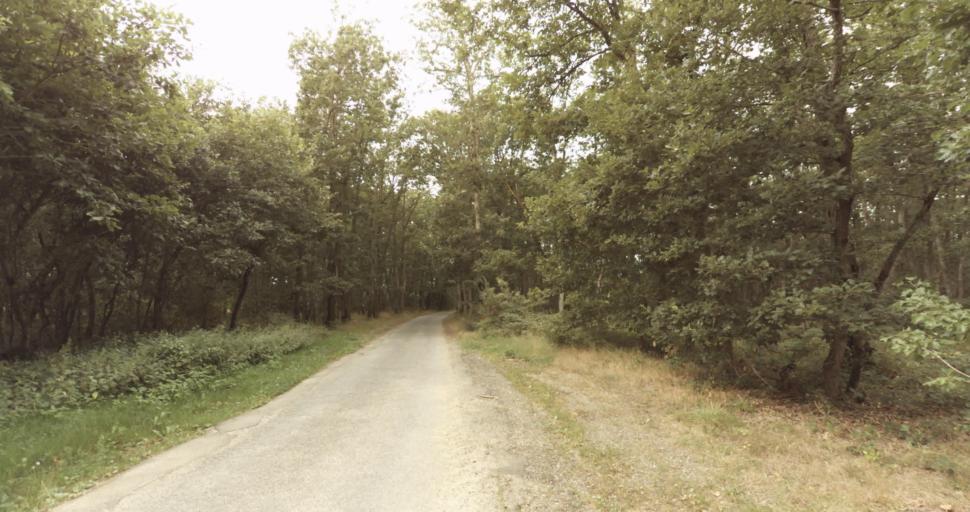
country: FR
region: Haute-Normandie
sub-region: Departement de l'Eure
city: Marcilly-sur-Eure
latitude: 48.8072
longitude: 1.3056
